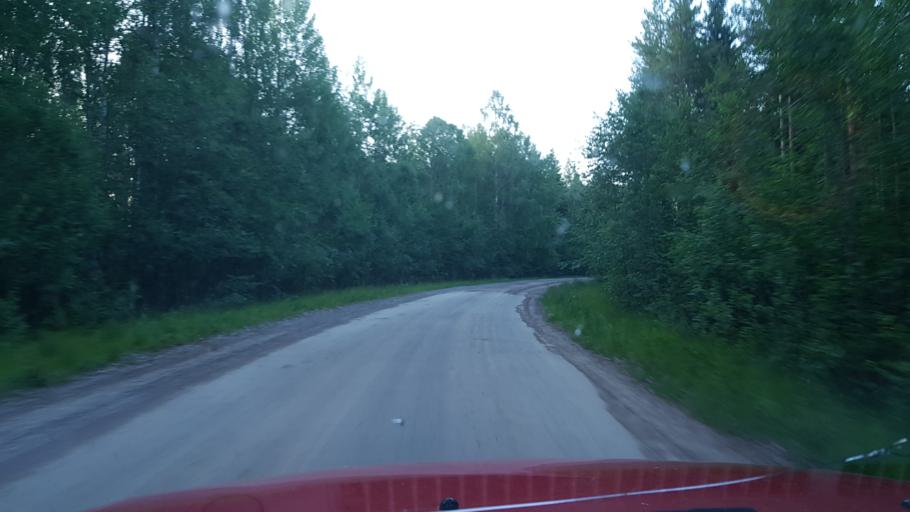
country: SE
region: Norrbotten
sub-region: Alvsbyns Kommun
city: AElvsbyn
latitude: 65.6976
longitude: 20.6701
